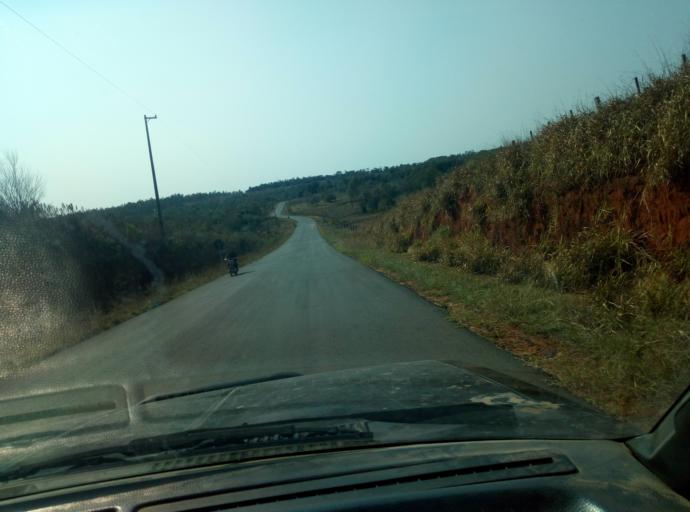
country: PY
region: Caaguazu
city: Carayao
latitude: -25.2639
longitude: -56.2870
